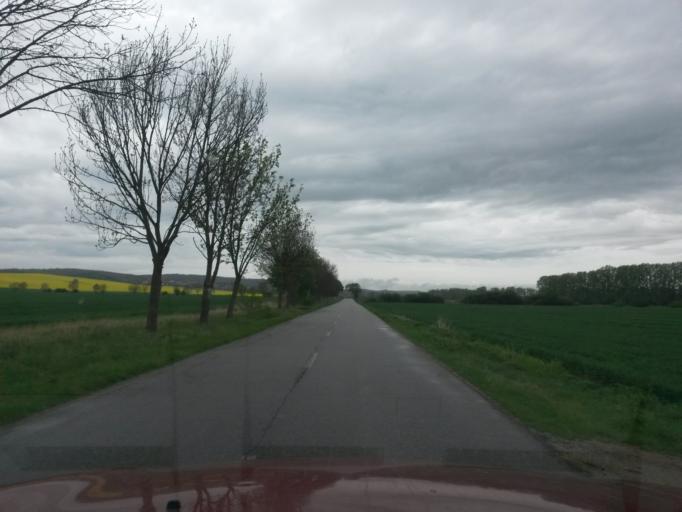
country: HU
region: Borsod-Abauj-Zemplen
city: Gonc
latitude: 48.5424
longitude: 21.2115
